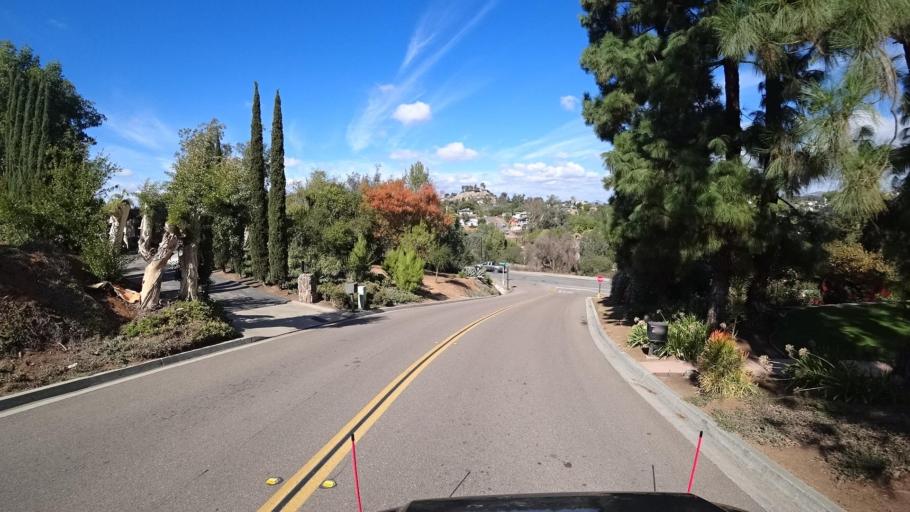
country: US
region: California
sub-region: San Diego County
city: Rancho San Diego
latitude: 32.7690
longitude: -116.9337
